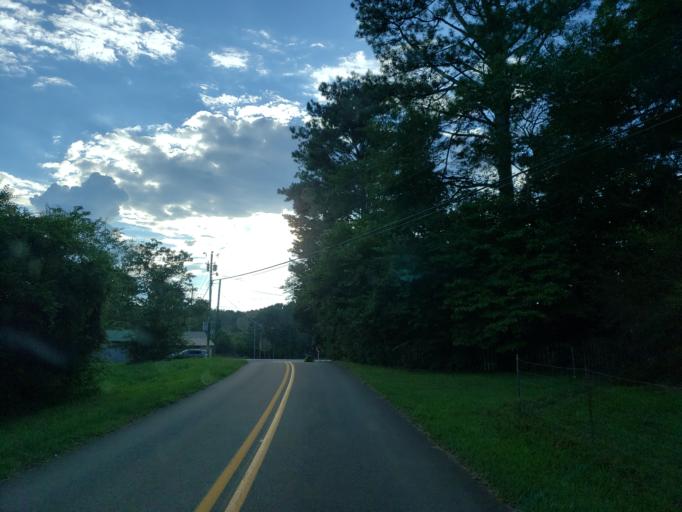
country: US
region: Georgia
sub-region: Cherokee County
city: Ball Ground
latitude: 34.3631
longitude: -84.4825
